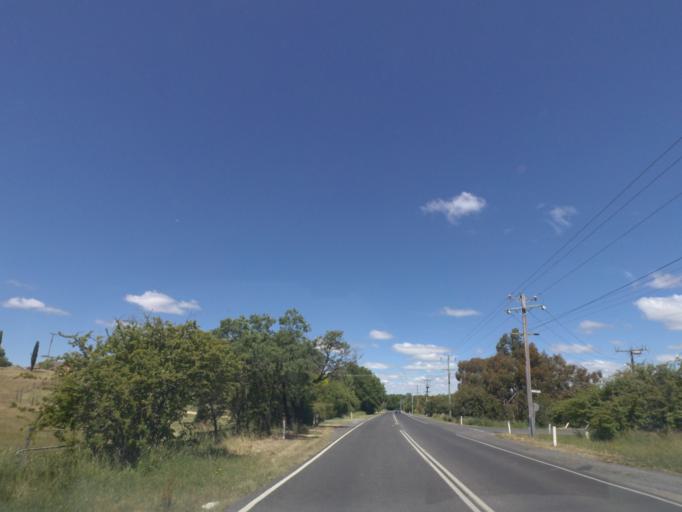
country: AU
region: Victoria
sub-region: Mount Alexander
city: Castlemaine
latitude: -37.2412
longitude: 144.4358
